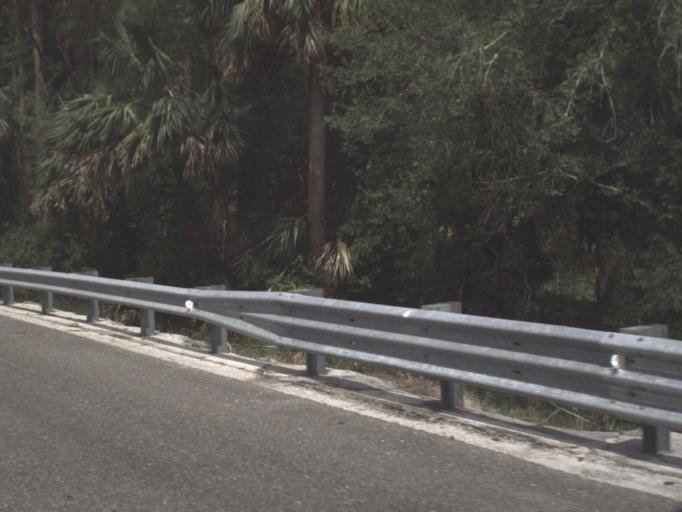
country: US
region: Florida
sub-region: Flagler County
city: Bunnell
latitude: 29.3607
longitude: -81.3115
